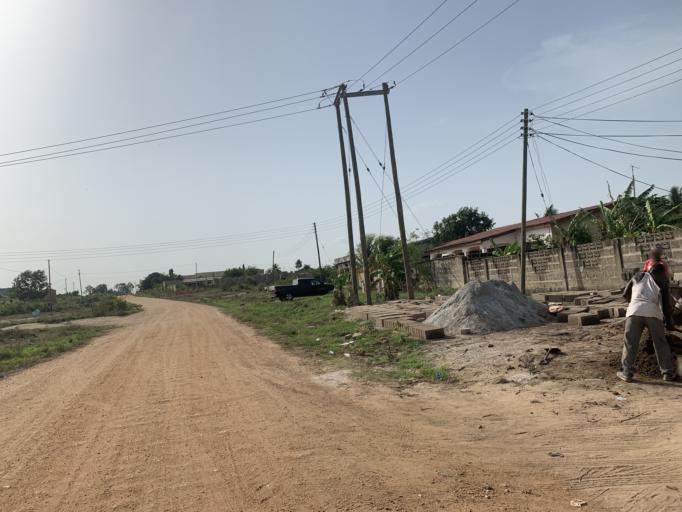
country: GH
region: Central
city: Winneba
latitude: 5.3640
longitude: -0.6426
